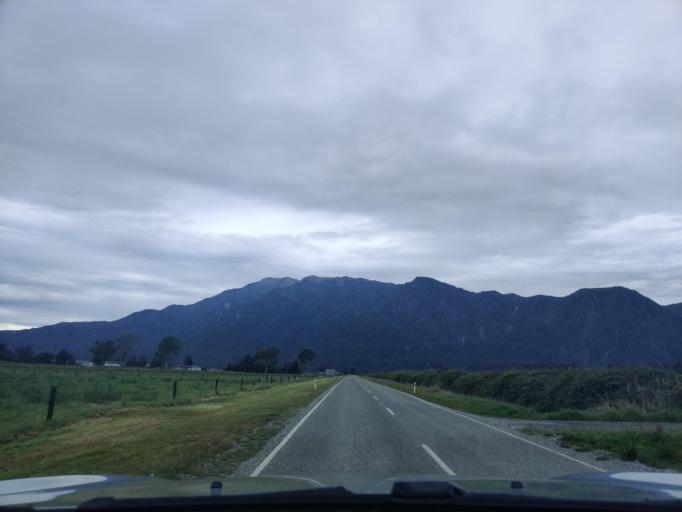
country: NZ
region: West Coast
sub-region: Westland District
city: Hokitika
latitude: -43.1534
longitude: 170.5989
